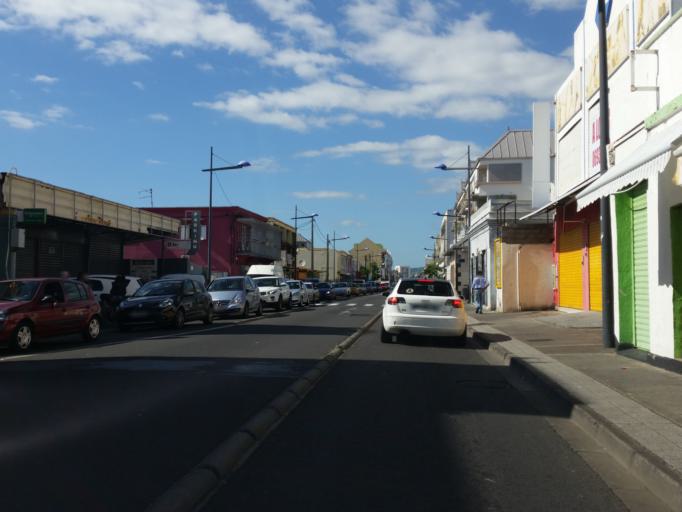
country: RE
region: Reunion
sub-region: Reunion
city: Saint-Denis
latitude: -20.8806
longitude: 55.4577
